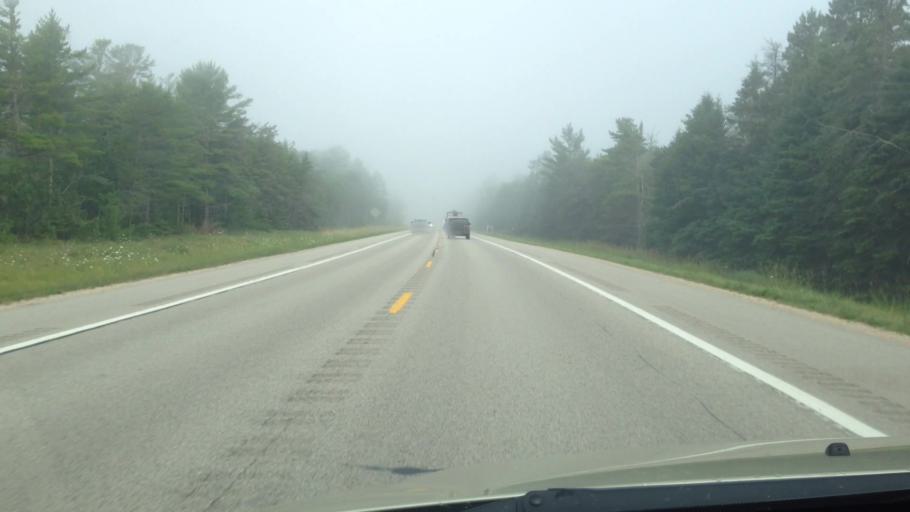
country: US
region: Michigan
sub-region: Luce County
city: Newberry
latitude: 46.0981
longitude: -85.4801
